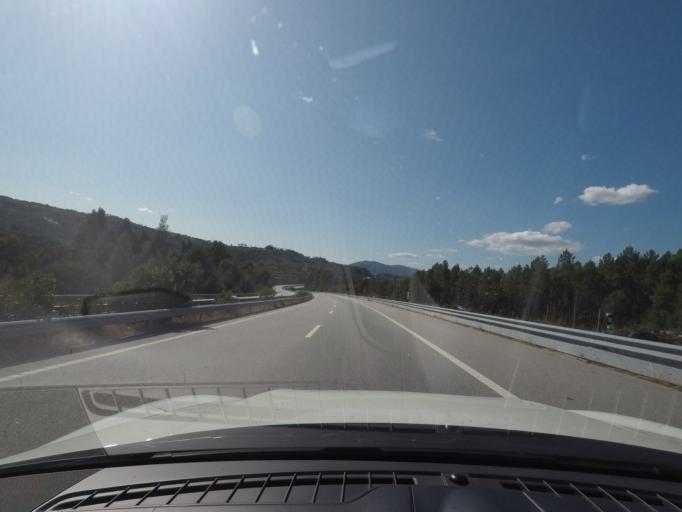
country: PT
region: Vila Real
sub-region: Mondim de Basto
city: Mondim de Basto
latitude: 41.4796
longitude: -7.8966
